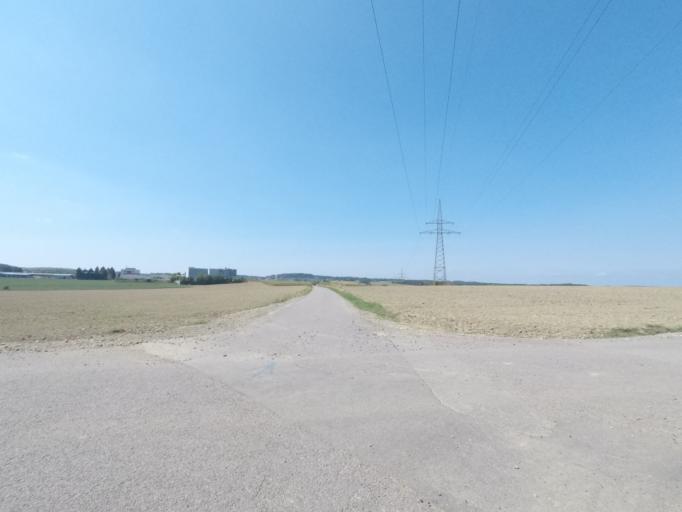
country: LU
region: Luxembourg
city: Capellen
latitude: 49.6242
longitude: 5.9893
